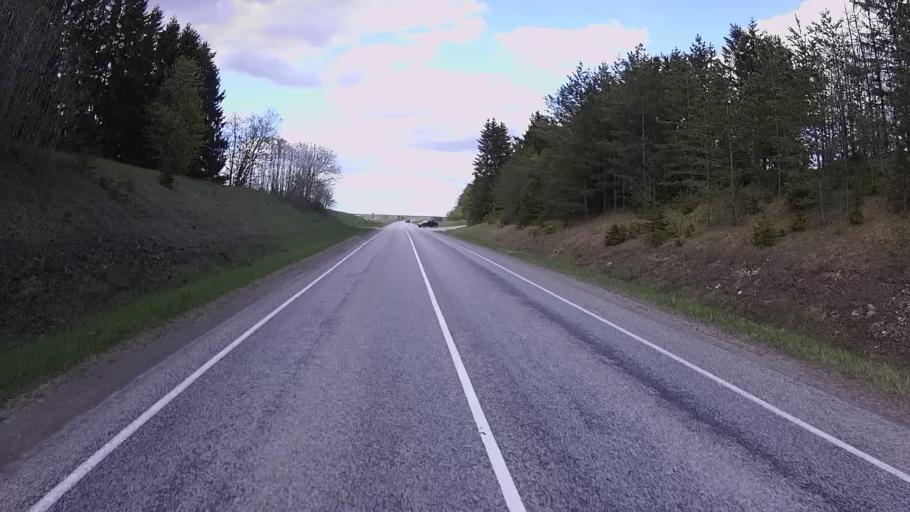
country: EE
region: Jogevamaa
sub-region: Jogeva linn
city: Jogeva
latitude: 58.7839
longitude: 26.4757
